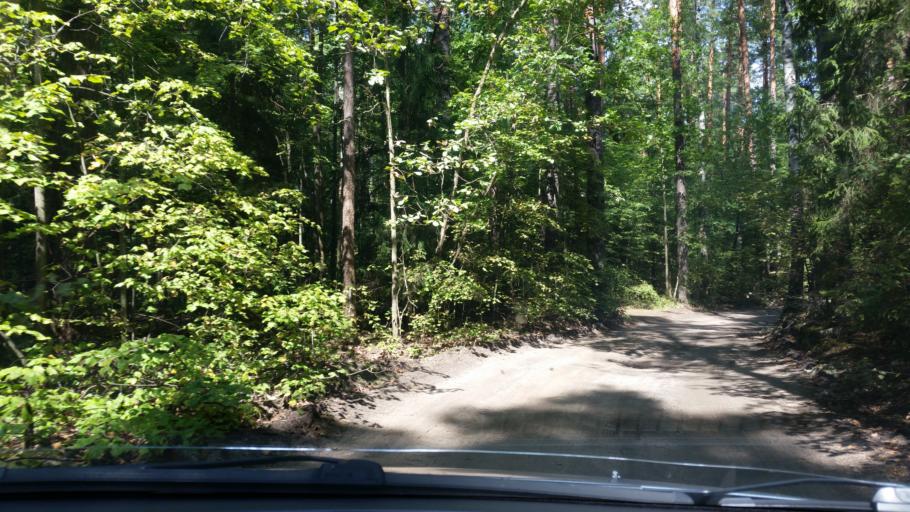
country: RU
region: Moskovskaya
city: Pushchino
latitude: 54.9072
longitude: 37.7160
